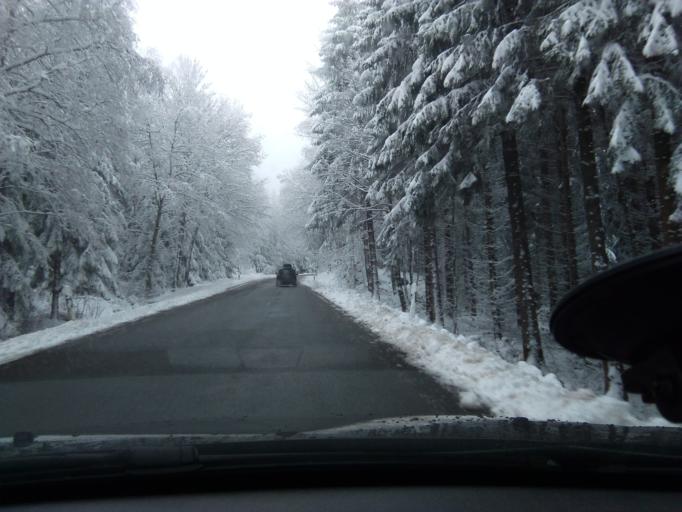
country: DE
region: Saxony
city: Markersbach
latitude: 50.5139
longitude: 12.8583
